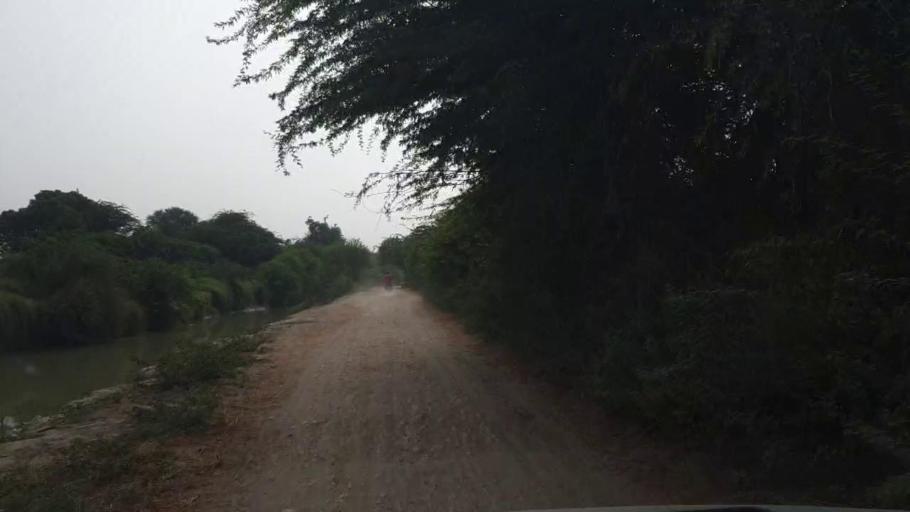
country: PK
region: Sindh
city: Matli
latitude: 24.9875
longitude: 68.7023
